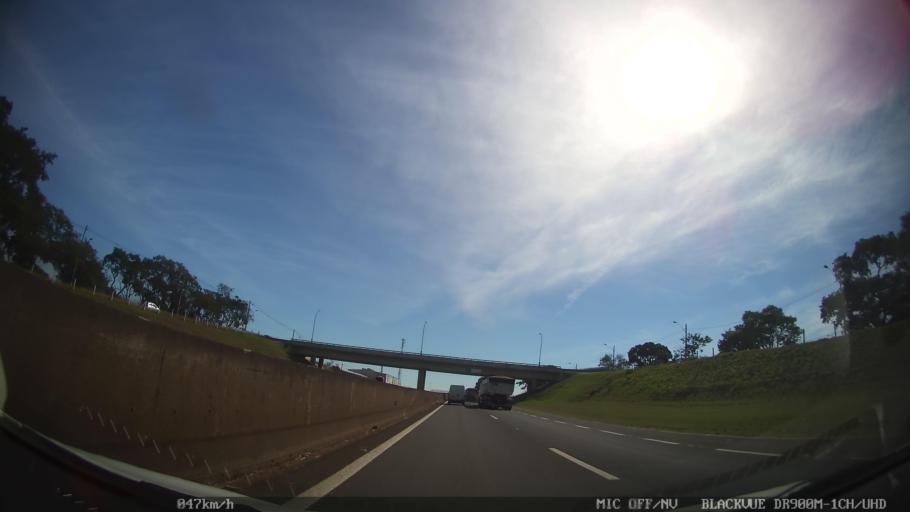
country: BR
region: Sao Paulo
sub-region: Porto Ferreira
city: Porto Ferreira
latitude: -21.8618
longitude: -47.4922
